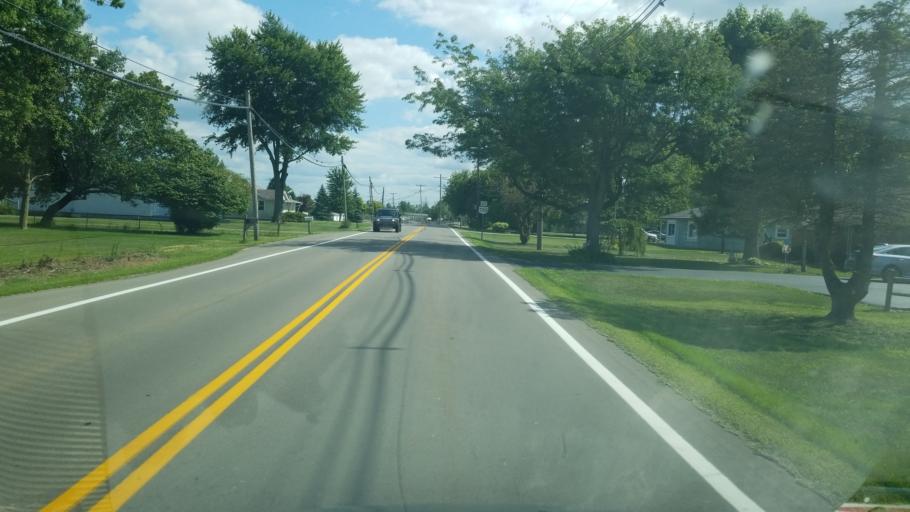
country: US
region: Ohio
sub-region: Logan County
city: Lakeview
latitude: 40.4794
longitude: -83.9236
